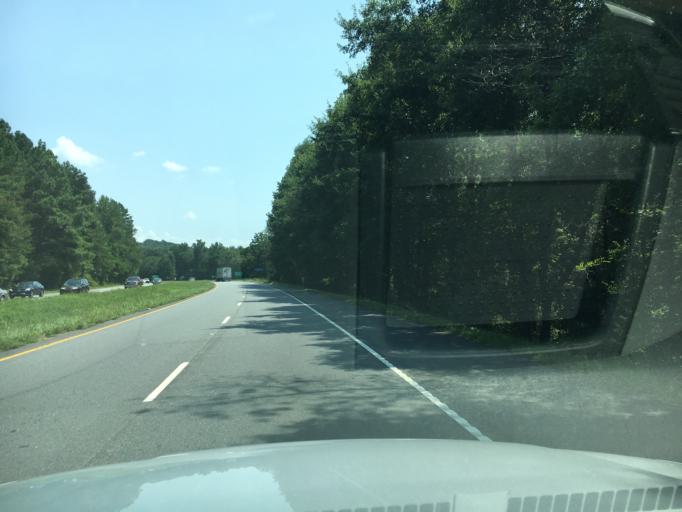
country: US
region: South Carolina
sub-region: Anderson County
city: Pendleton
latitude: 34.6491
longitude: -82.8075
